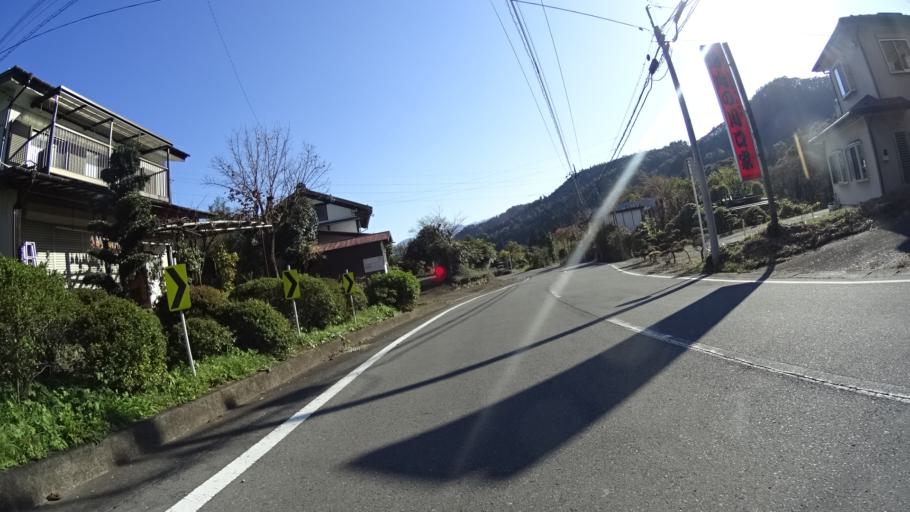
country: JP
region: Yamanashi
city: Uenohara
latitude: 35.6523
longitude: 139.1207
